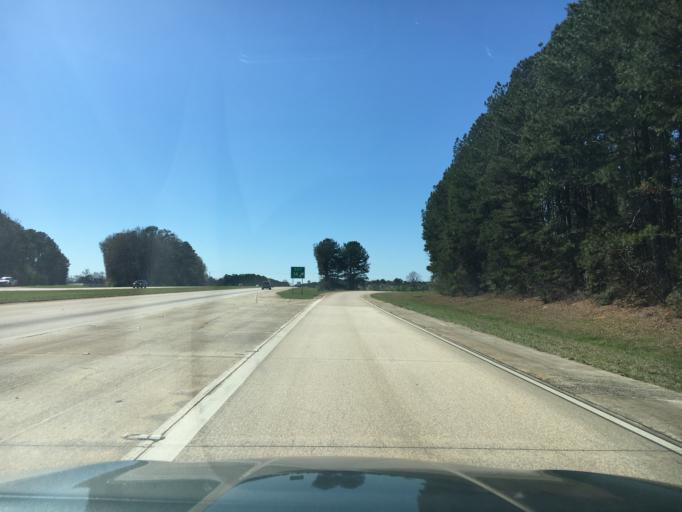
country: US
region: Georgia
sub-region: Troup County
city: La Grange
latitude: 33.0030
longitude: -85.0082
